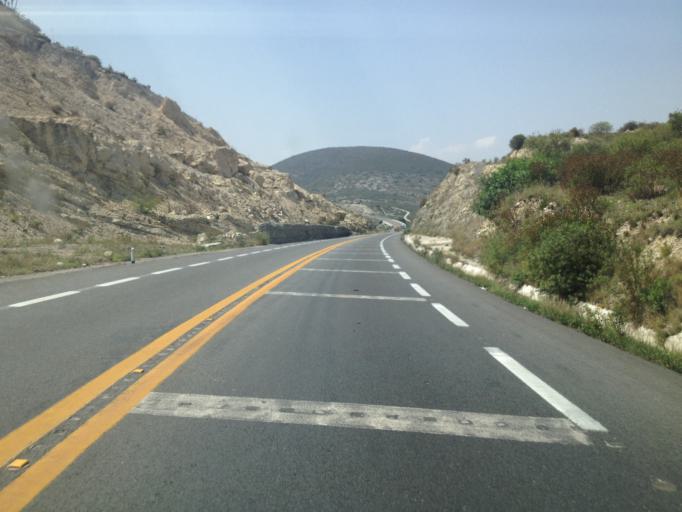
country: MX
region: Puebla
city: Chapuco
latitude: 18.6590
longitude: -97.4566
